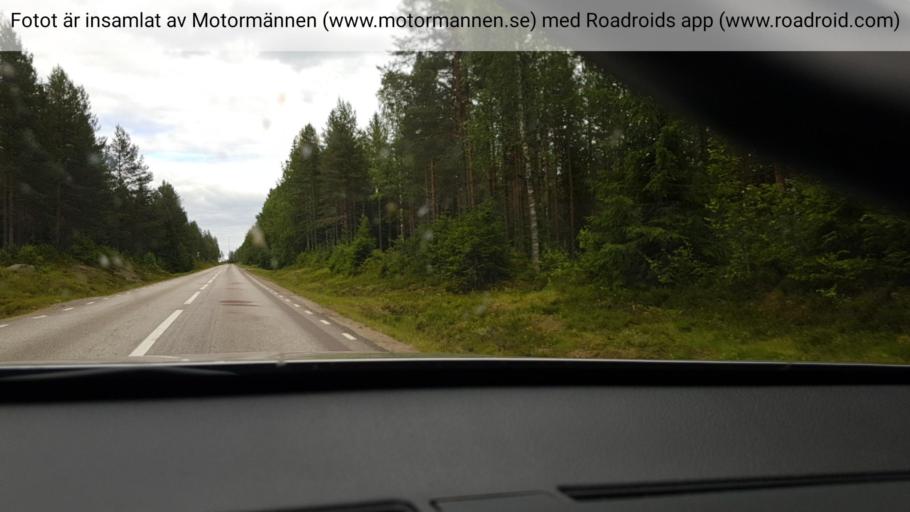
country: NO
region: Hedmark
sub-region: Trysil
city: Innbygda
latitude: 61.0305
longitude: 12.4796
